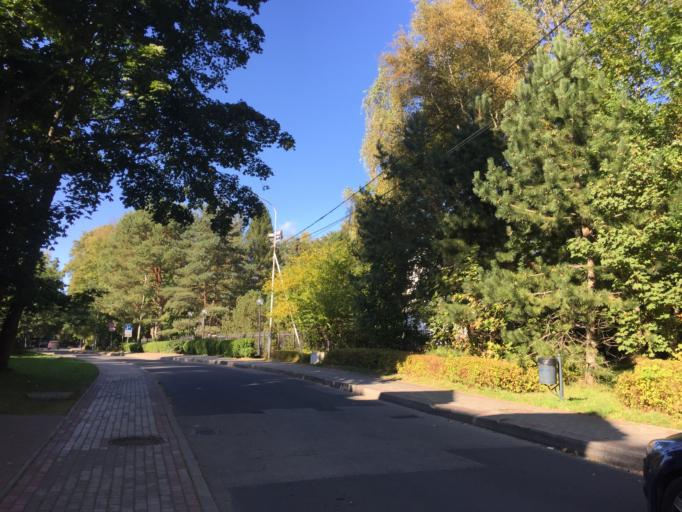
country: RU
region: Kaliningrad
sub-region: Gorod Svetlogorsk
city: Svetlogorsk
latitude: 54.9435
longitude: 20.1630
